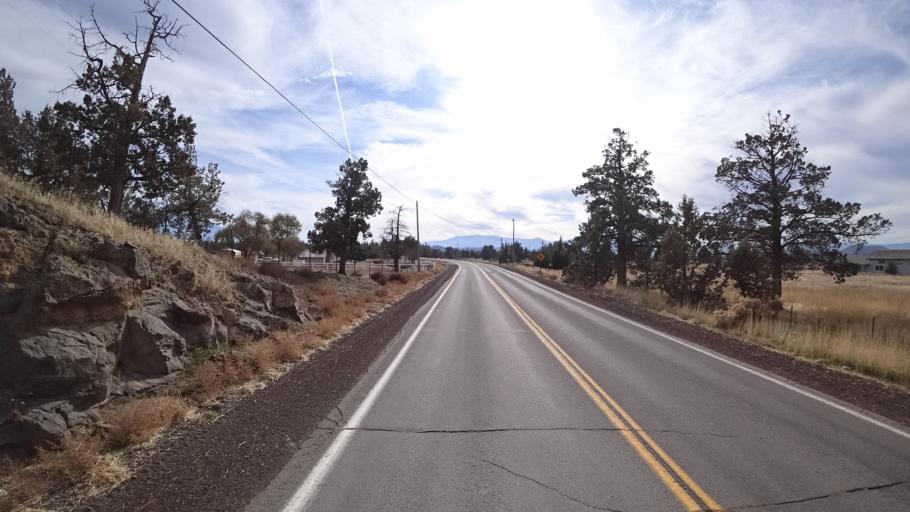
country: US
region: California
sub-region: Siskiyou County
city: Montague
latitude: 41.6118
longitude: -122.3998
